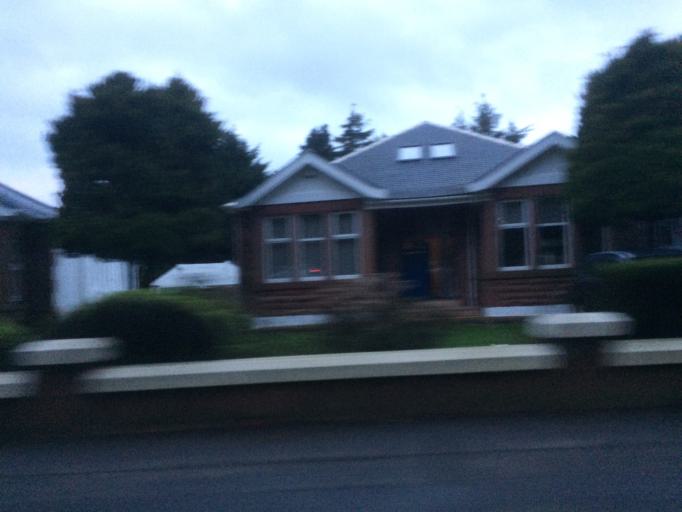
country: GB
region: Scotland
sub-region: East Renfrewshire
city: Newton Mearns
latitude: 55.7775
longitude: -4.3262
